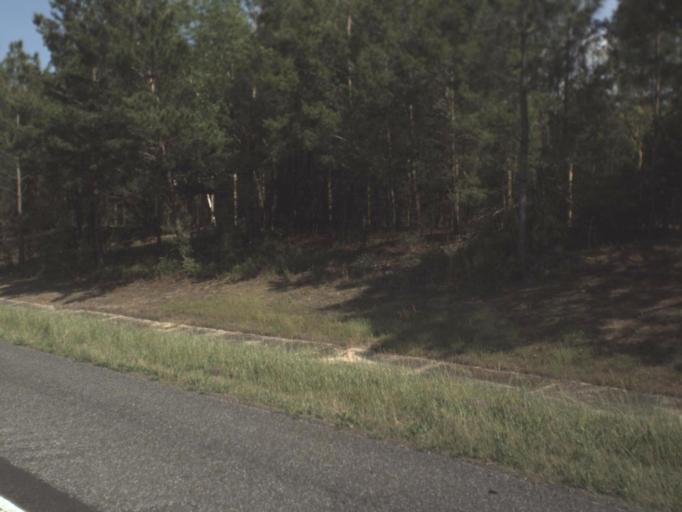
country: US
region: Florida
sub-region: Santa Rosa County
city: East Milton
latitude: 30.6793
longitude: -86.8136
